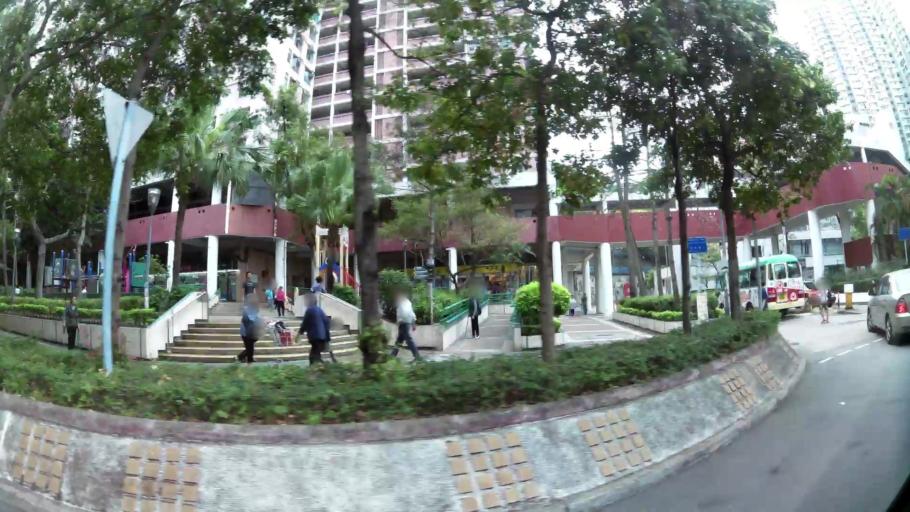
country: HK
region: Kowloon City
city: Kowloon
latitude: 22.3135
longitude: 114.2300
